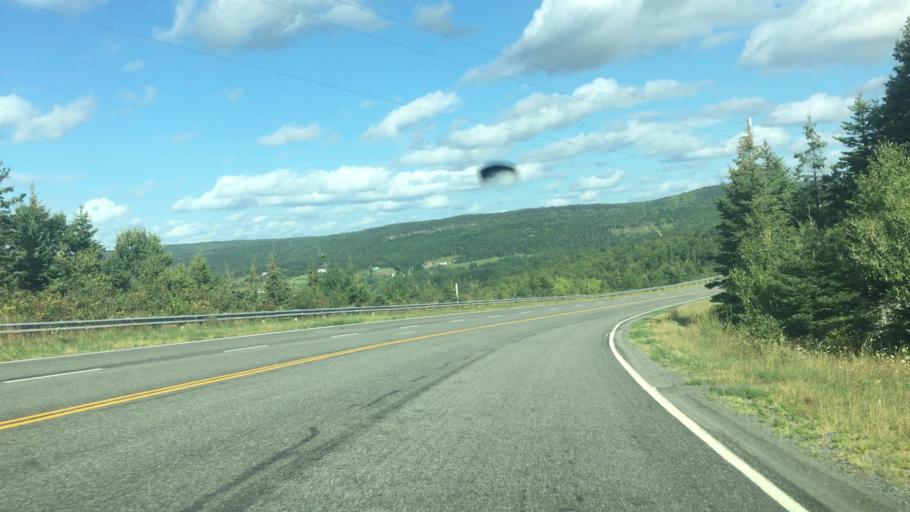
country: CA
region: Nova Scotia
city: Sydney
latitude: 45.8154
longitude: -60.6904
